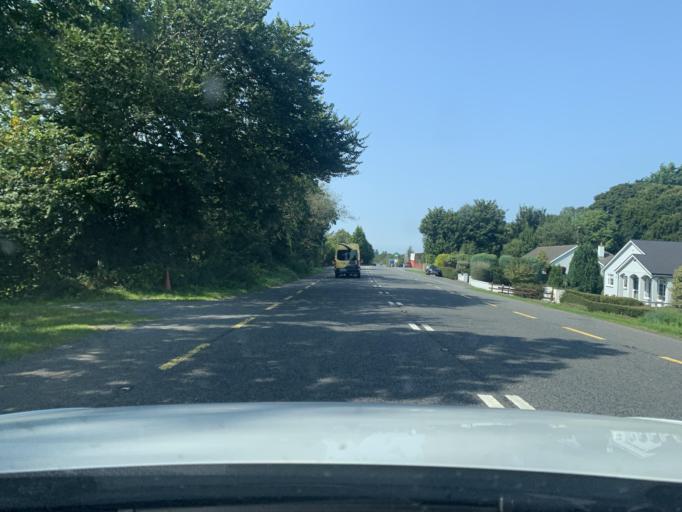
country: IE
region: Leinster
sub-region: An Iarmhi
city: Athlone
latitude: 53.4478
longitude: -7.9836
